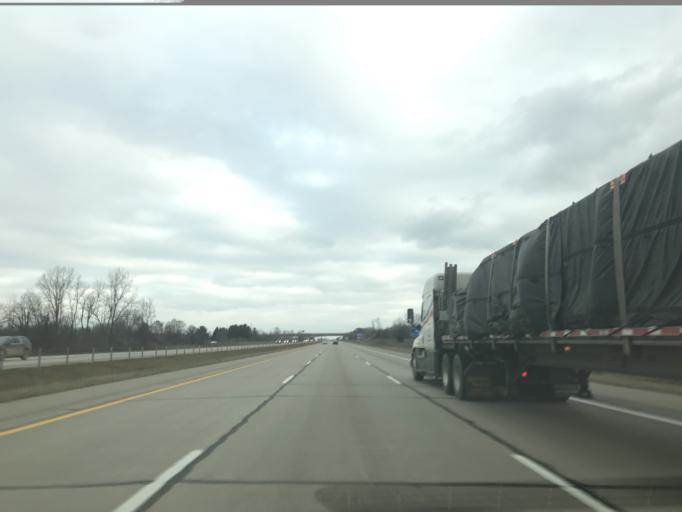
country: US
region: Michigan
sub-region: Eaton County
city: Waverly
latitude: 42.7214
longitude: -84.6688
